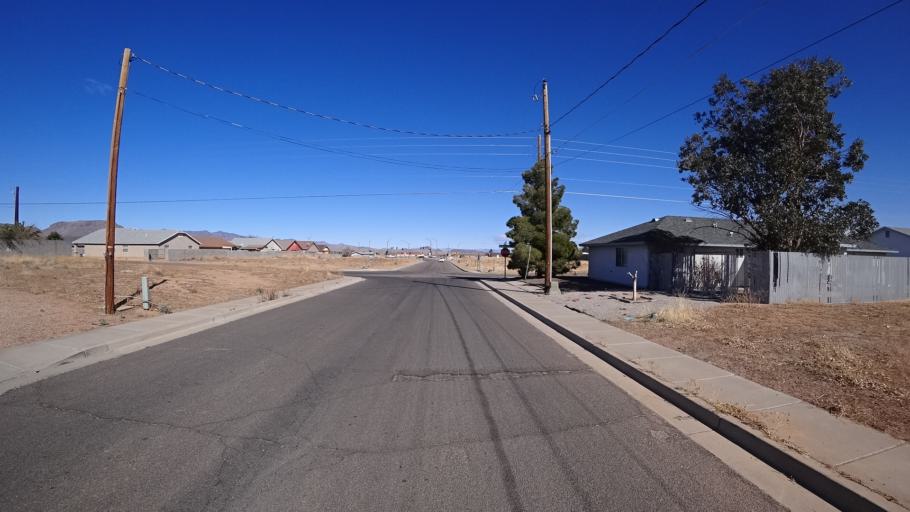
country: US
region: Arizona
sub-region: Mohave County
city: New Kingman-Butler
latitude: 35.2207
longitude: -113.9985
